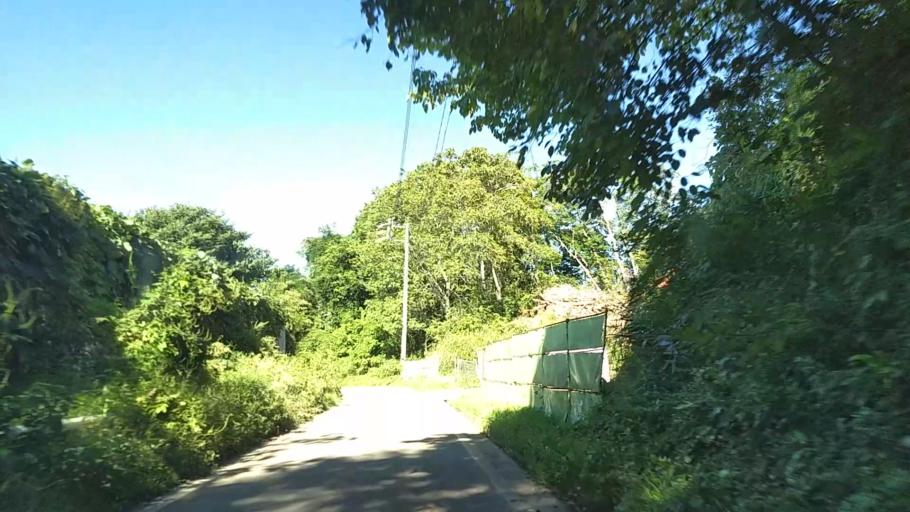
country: JP
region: Nagano
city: Nagano-shi
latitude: 36.5874
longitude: 138.0888
